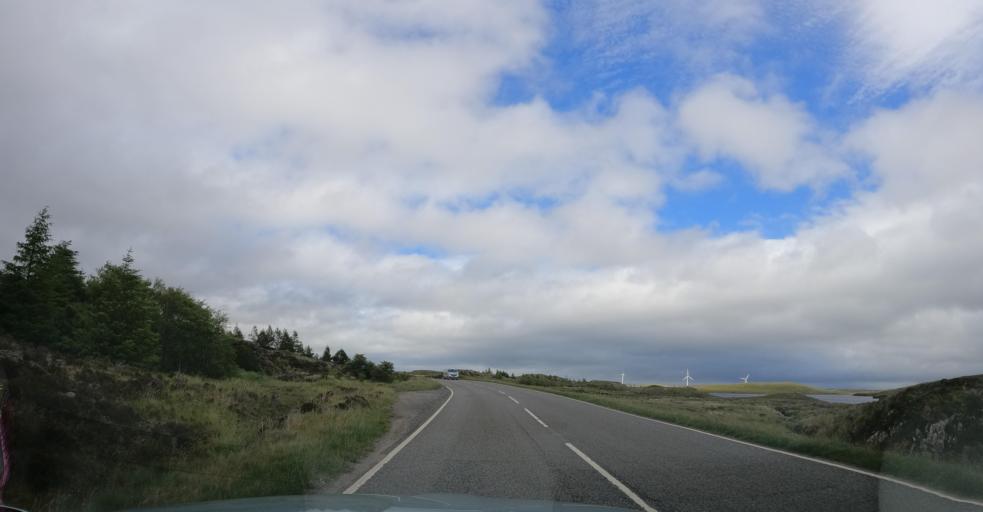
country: GB
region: Scotland
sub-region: Eilean Siar
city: Stornoway
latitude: 58.1748
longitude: -6.4691
